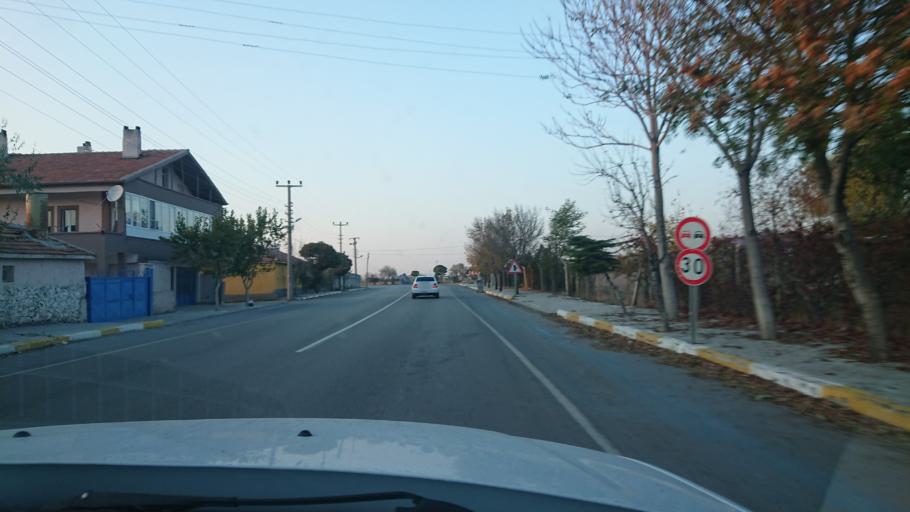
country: TR
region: Aksaray
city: Aksaray
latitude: 38.3088
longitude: 34.0666
